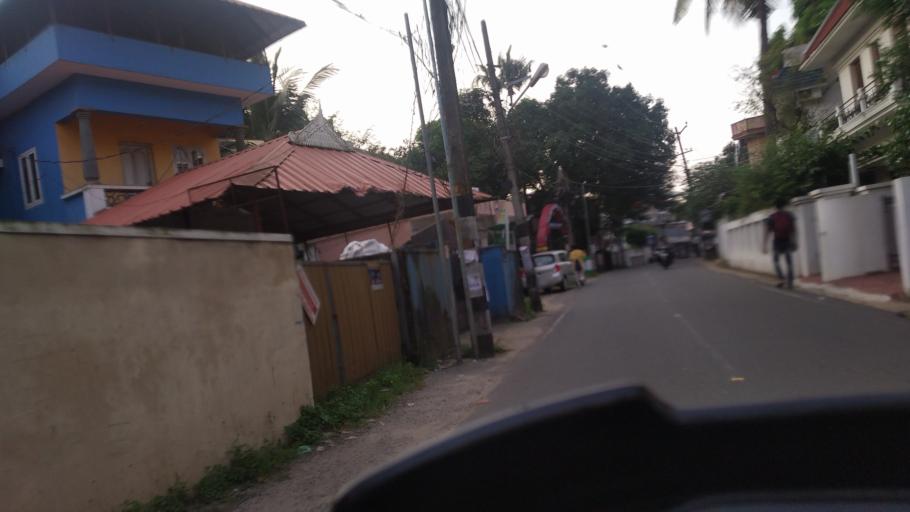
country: IN
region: Kerala
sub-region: Ernakulam
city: Elur
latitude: 10.0240
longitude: 76.2994
